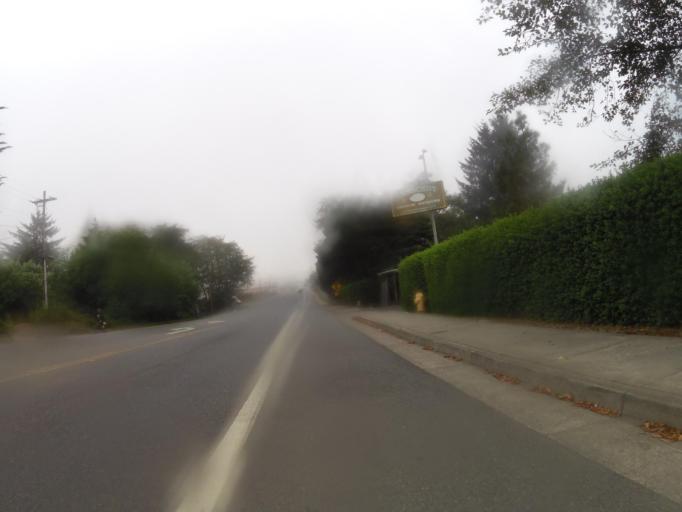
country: US
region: California
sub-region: Del Norte County
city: Crescent City
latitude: 41.7728
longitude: -124.1959
